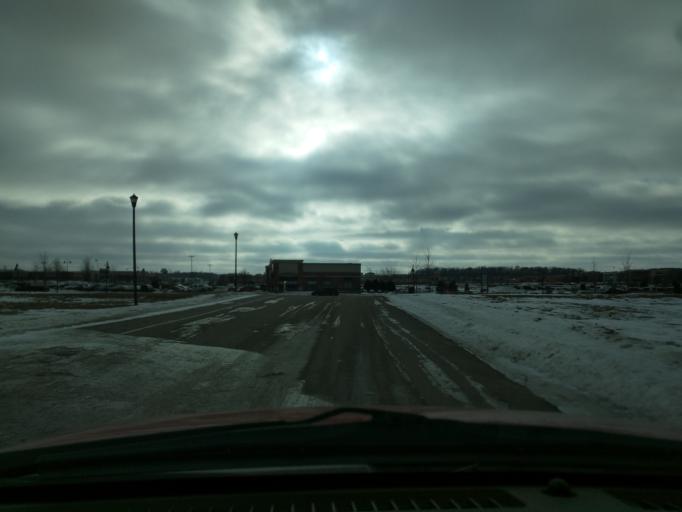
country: US
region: Minnesota
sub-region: Olmsted County
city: Rochester
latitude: 43.9598
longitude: -92.4624
